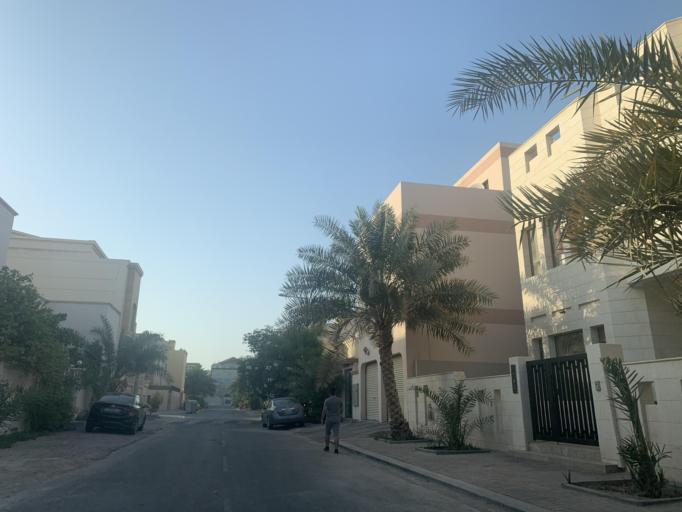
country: BH
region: Manama
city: Jidd Hafs
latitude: 26.1976
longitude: 50.5297
